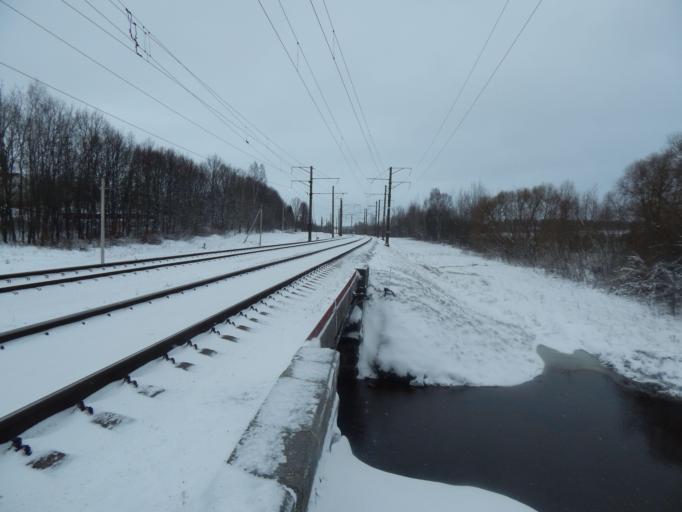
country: BY
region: Minsk
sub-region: Minski Rayon
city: Krasnaye
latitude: 54.1305
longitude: 27.1078
